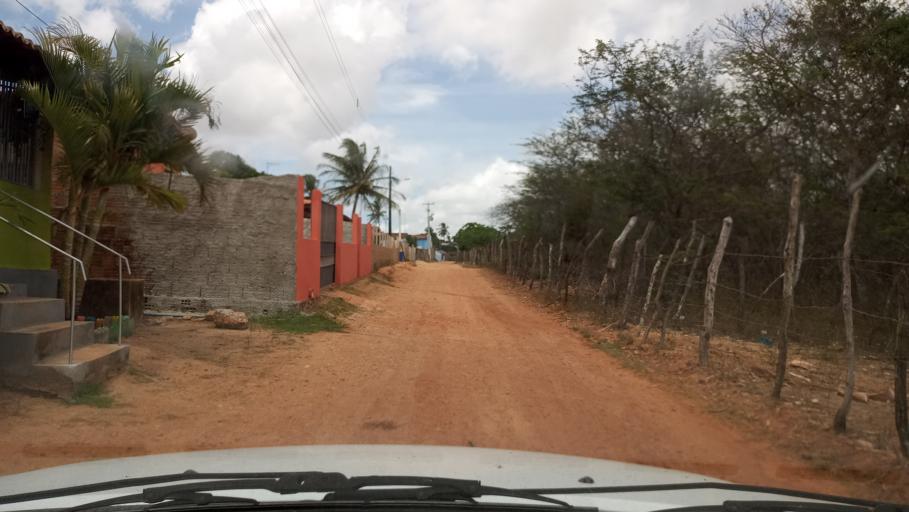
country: BR
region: Rio Grande do Norte
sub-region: Goianinha
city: Goianinha
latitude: -6.2942
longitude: -35.2799
